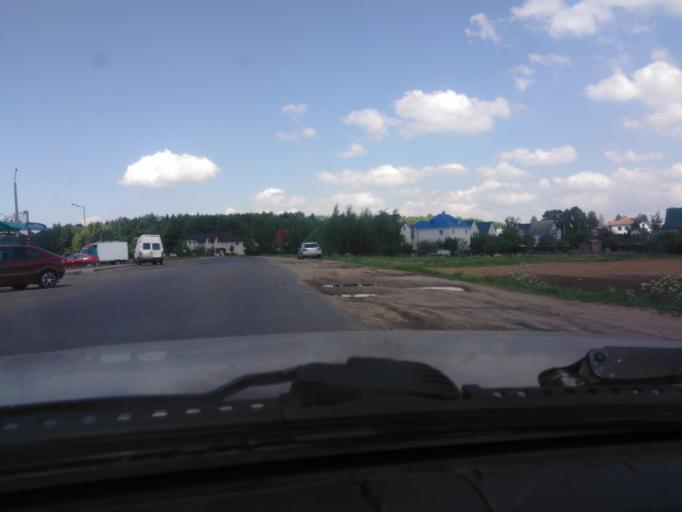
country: BY
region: Mogilev
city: Palykavichy Pyershyya
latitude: 53.9516
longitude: 30.3723
